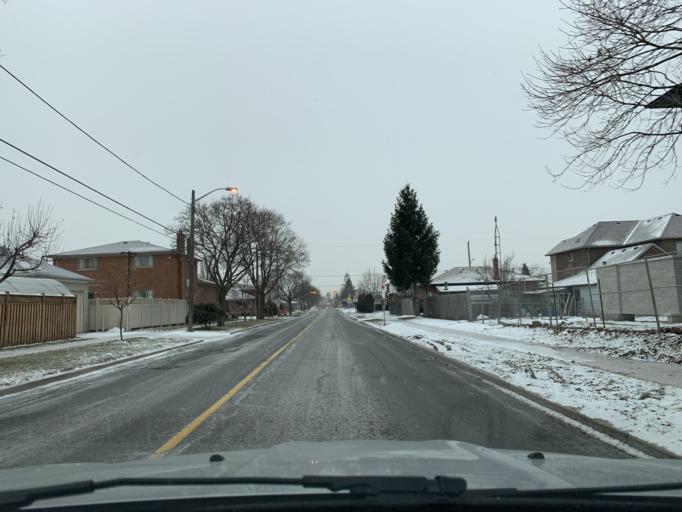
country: CA
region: Ontario
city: North York
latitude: 43.7337
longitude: -79.4695
